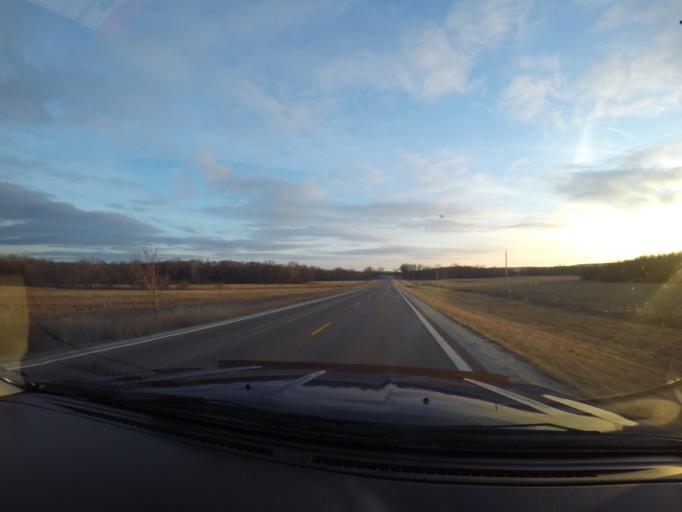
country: US
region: Kansas
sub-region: Chase County
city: Cottonwood Falls
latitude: 38.4847
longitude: -96.5573
